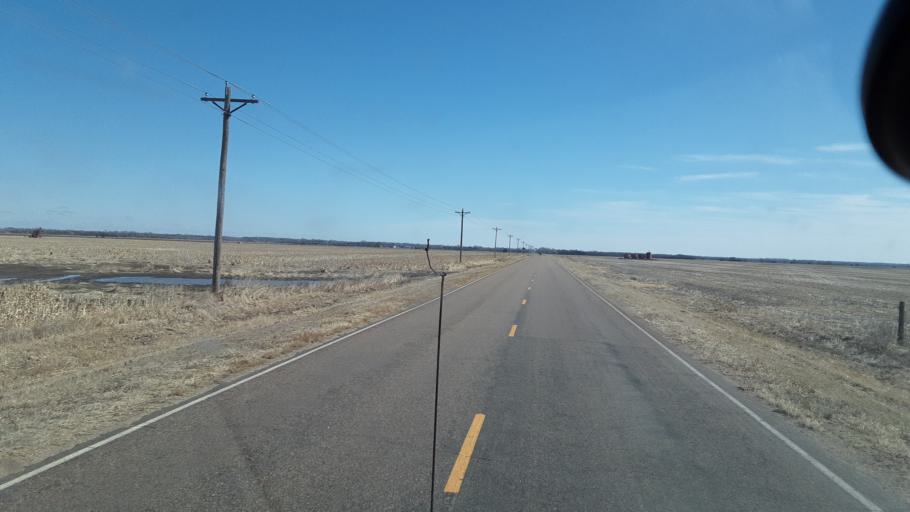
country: US
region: Kansas
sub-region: Reno County
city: Nickerson
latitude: 38.2175
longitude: -98.1030
